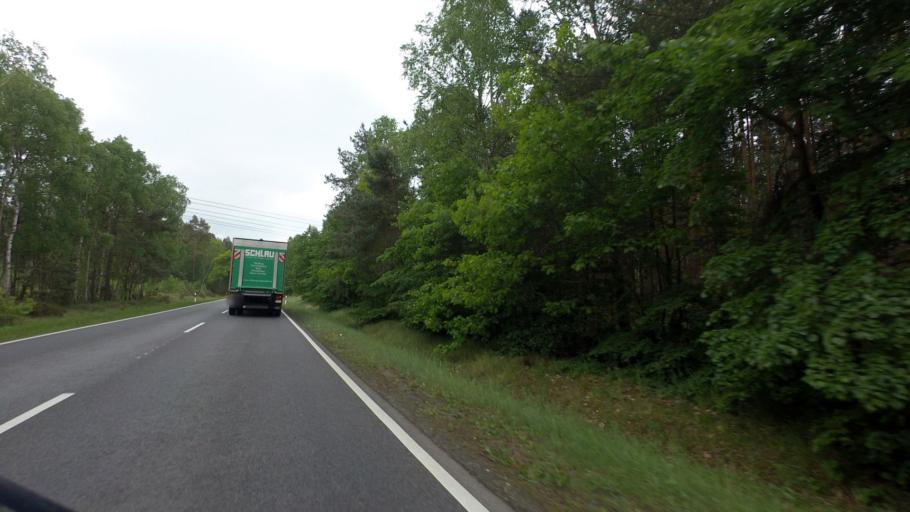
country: DE
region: Brandenburg
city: Furstenberg
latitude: 53.2111
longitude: 13.1292
